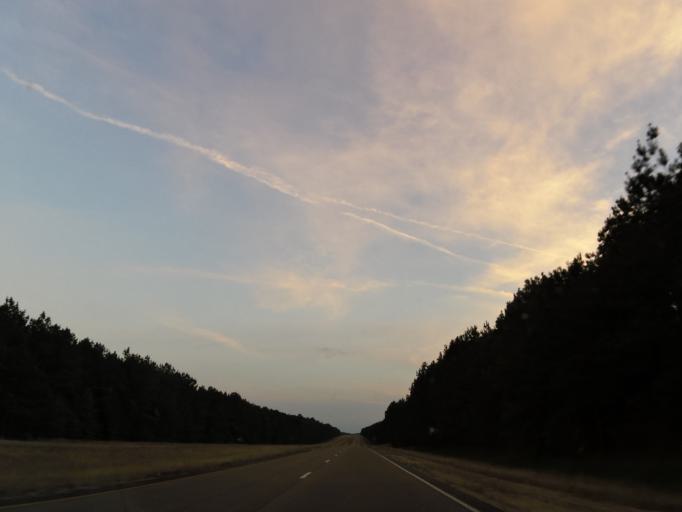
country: US
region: Mississippi
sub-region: Lauderdale County
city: Meridian Station
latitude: 32.6756
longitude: -88.4909
